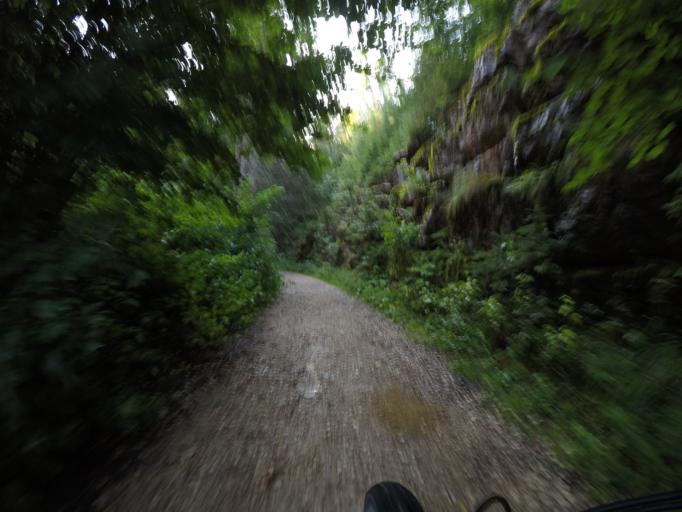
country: IT
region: Veneto
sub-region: Provincia di Vicenza
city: Asiago
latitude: 45.8530
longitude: 11.5159
